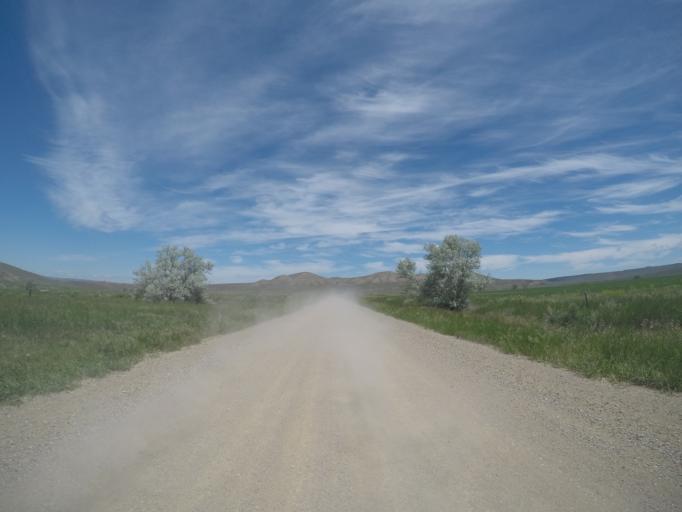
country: US
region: Montana
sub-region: Carbon County
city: Red Lodge
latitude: 45.2264
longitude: -108.8423
